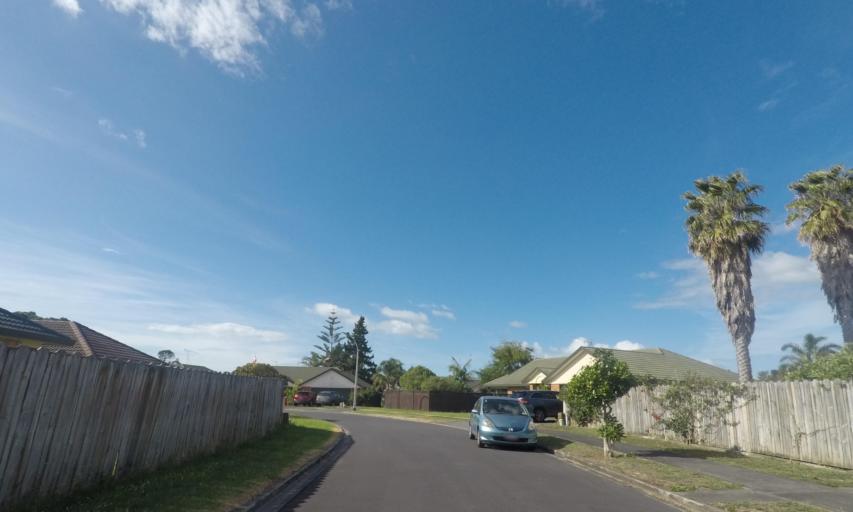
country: NZ
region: Auckland
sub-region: Auckland
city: Pakuranga
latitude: -36.9191
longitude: 174.8967
